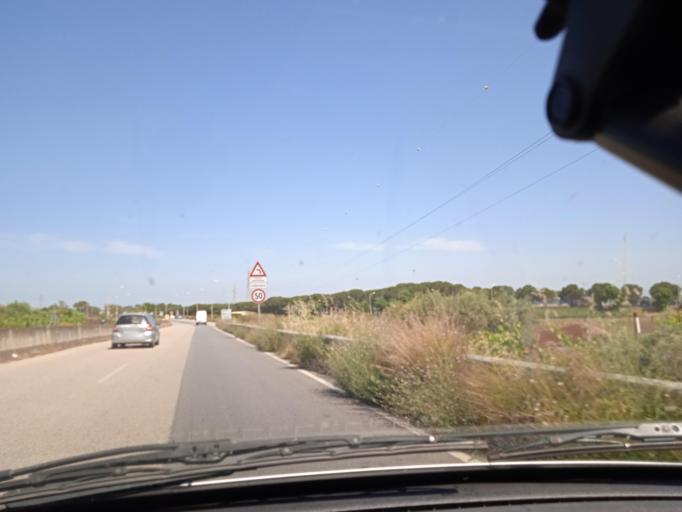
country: IT
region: Sicily
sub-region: Messina
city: Milazzo
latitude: 38.1955
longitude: 15.2557
